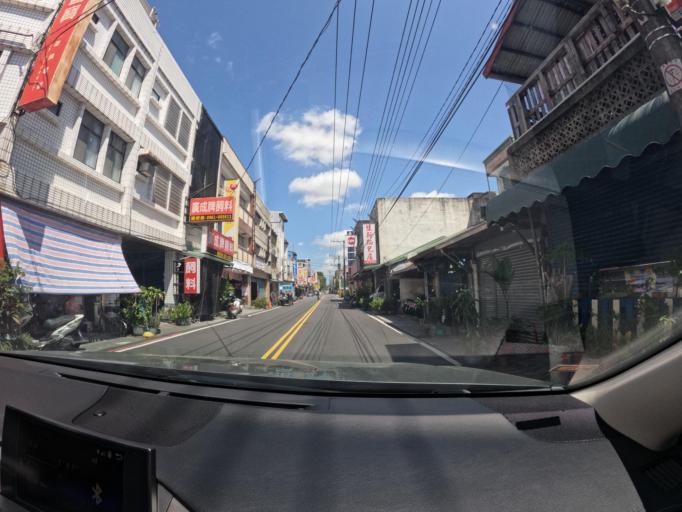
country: TW
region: Taiwan
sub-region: Hualien
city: Hualian
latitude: 23.6667
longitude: 121.4241
